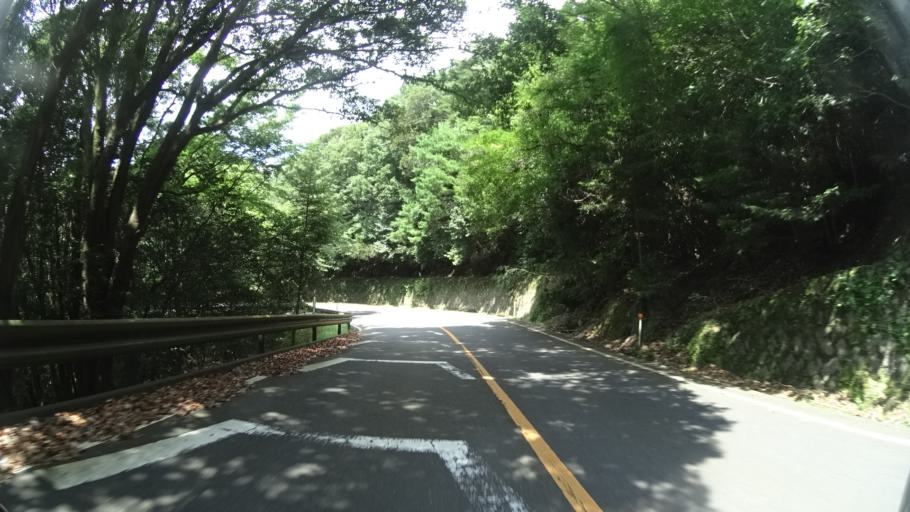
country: JP
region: Miyazaki
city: Kobayashi
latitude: 31.9032
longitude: 130.8471
